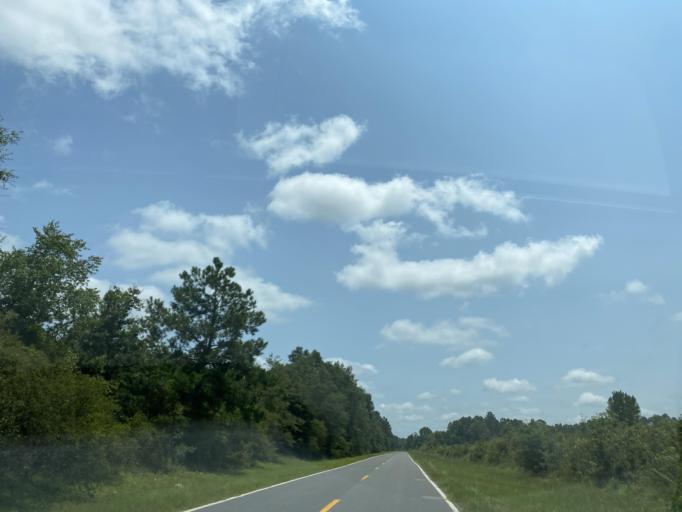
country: US
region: Georgia
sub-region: Telfair County
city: Lumber City
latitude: 31.9553
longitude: -82.6968
